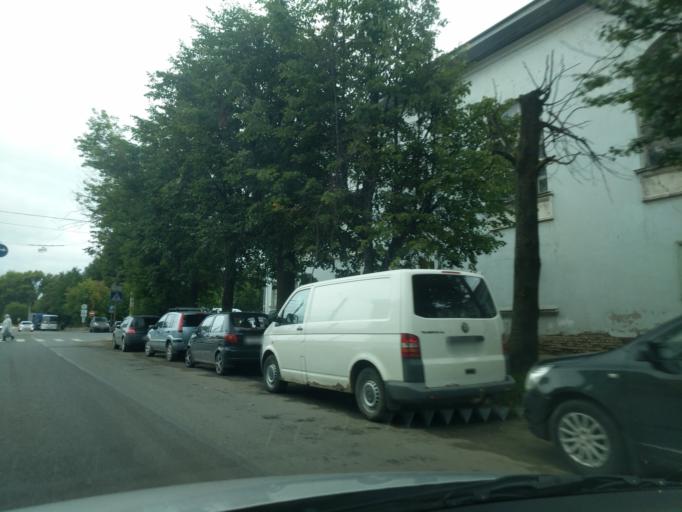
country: RU
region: Kirov
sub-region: Kirovo-Chepetskiy Rayon
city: Kirov
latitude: 58.6361
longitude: 49.6119
